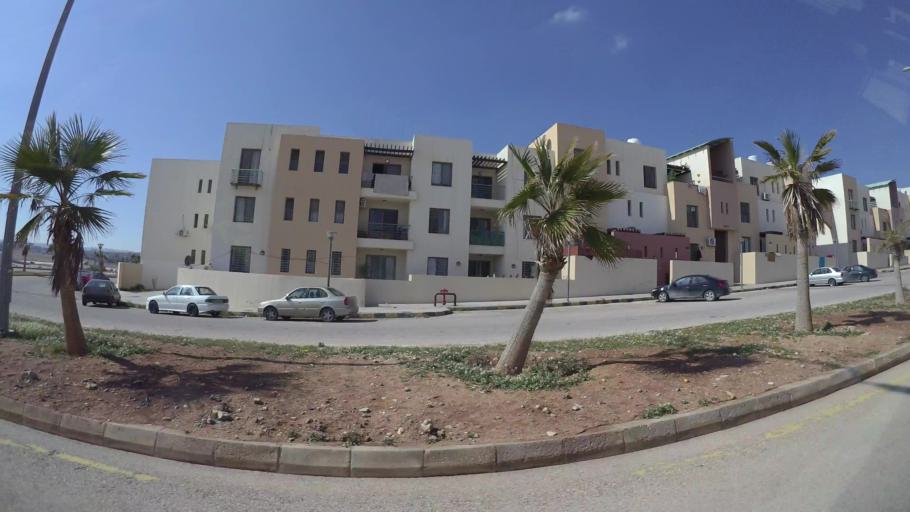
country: JO
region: Zarqa
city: Zarqa
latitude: 32.0704
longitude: 36.1122
